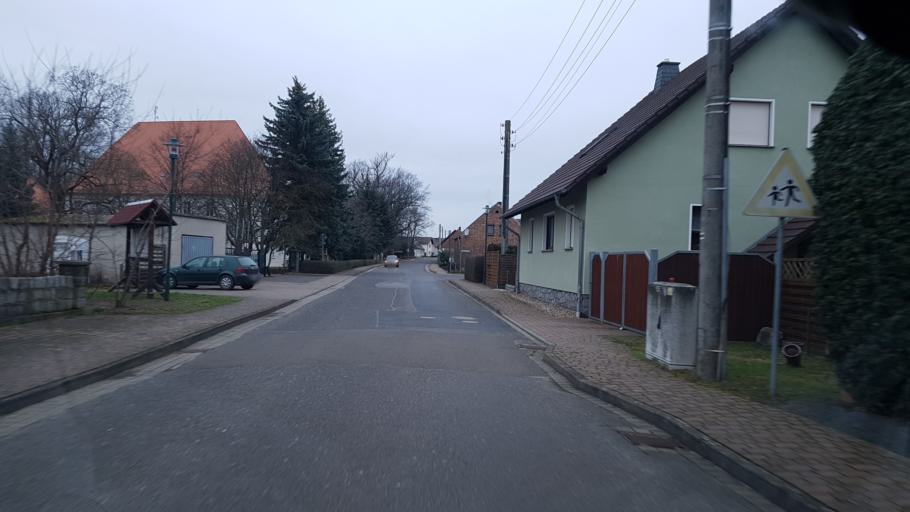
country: DE
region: Brandenburg
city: Herzberg
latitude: 51.7149
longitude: 13.2994
